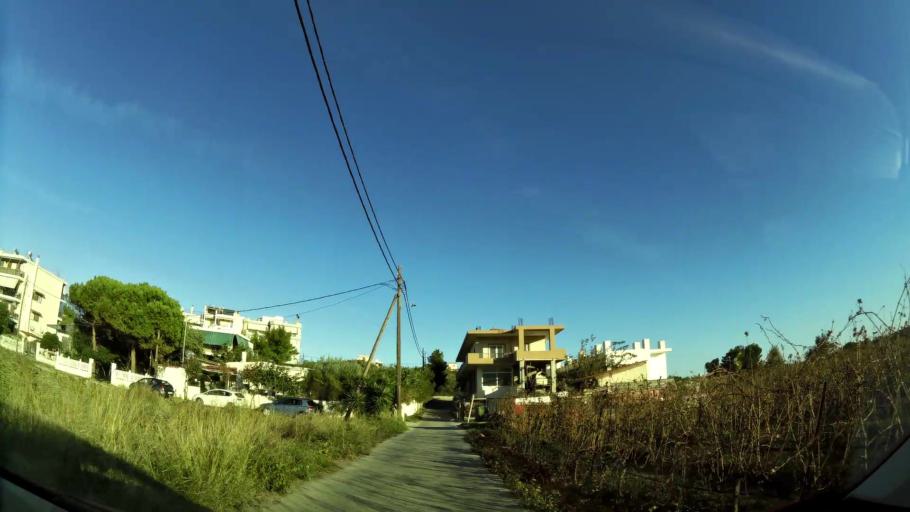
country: GR
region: Attica
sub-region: Nomarchia Anatolikis Attikis
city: Rafina
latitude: 38.0110
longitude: 24.0123
